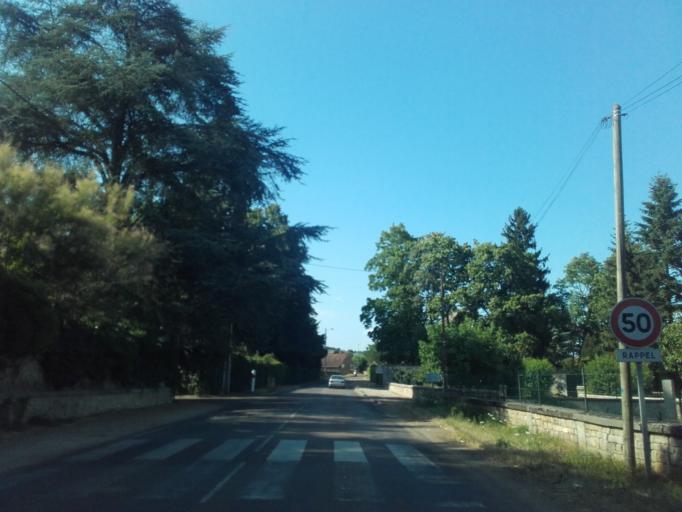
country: FR
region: Bourgogne
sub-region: Departement de Saone-et-Loire
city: Givry
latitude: 46.7725
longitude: 4.7380
